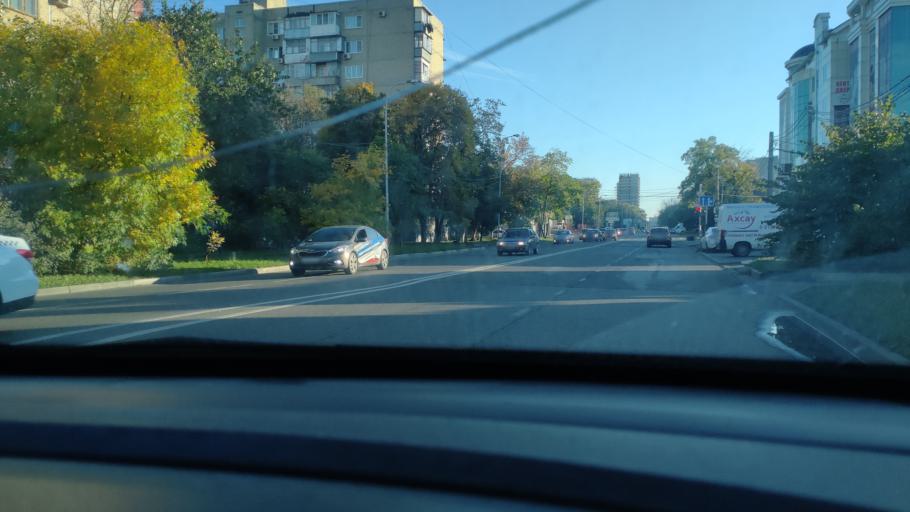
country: RU
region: Krasnodarskiy
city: Krasnodar
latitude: 45.0487
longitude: 38.9697
